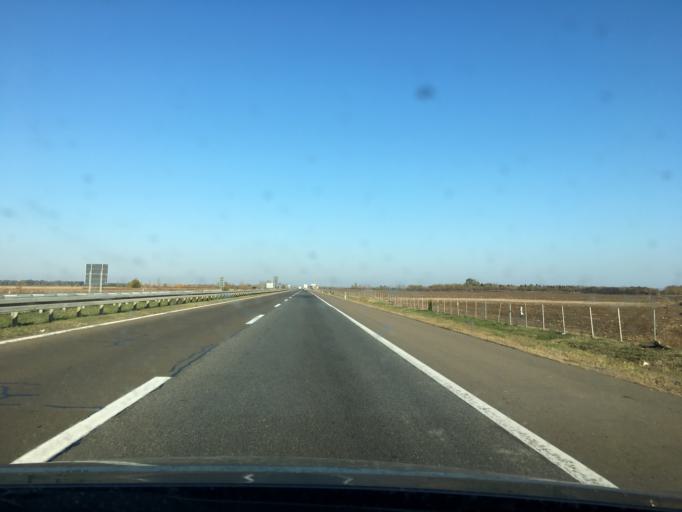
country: RS
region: Autonomna Pokrajina Vojvodina
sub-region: Sremski Okrug
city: Stara Pazova
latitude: 45.0134
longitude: 20.1976
